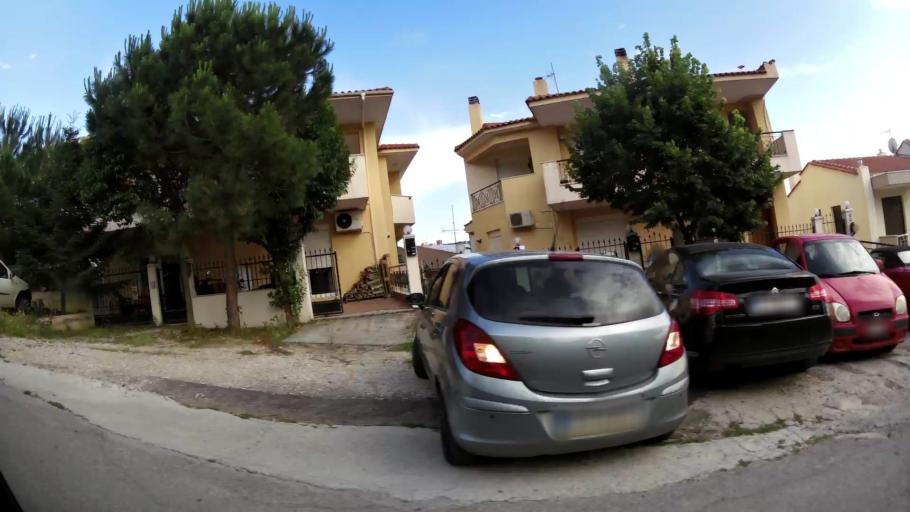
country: GR
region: Central Macedonia
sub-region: Nomos Thessalonikis
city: Pefka
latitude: 40.6577
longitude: 23.0026
